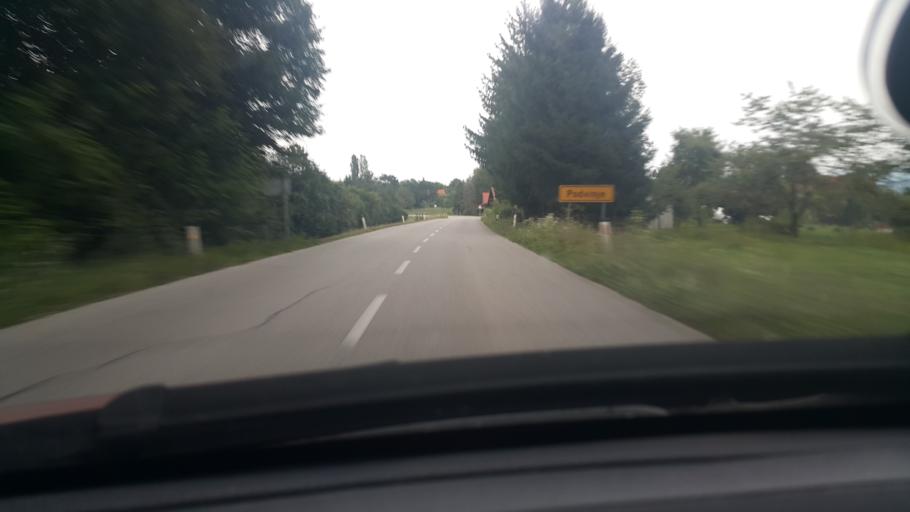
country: SI
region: Brezice
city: Brezice
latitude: 45.9195
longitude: 15.6647
